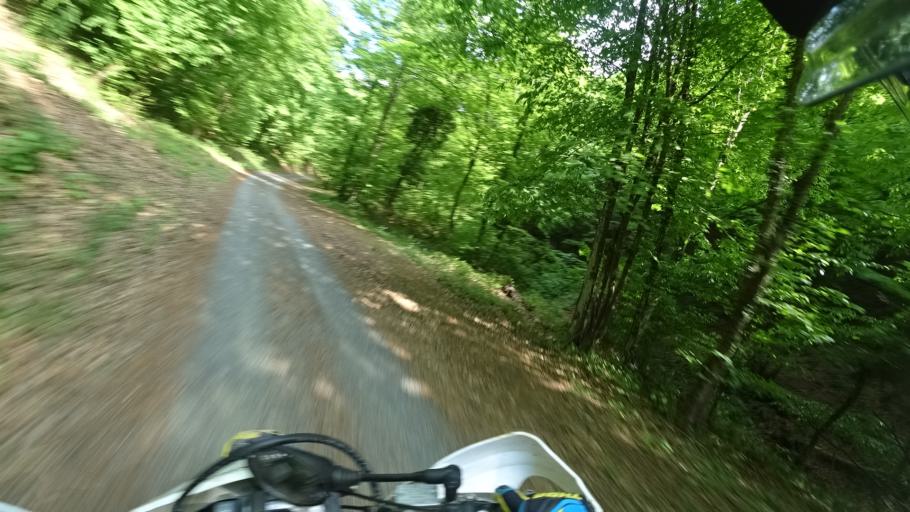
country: HR
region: Grad Zagreb
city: Kasina
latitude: 45.9327
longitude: 15.9464
